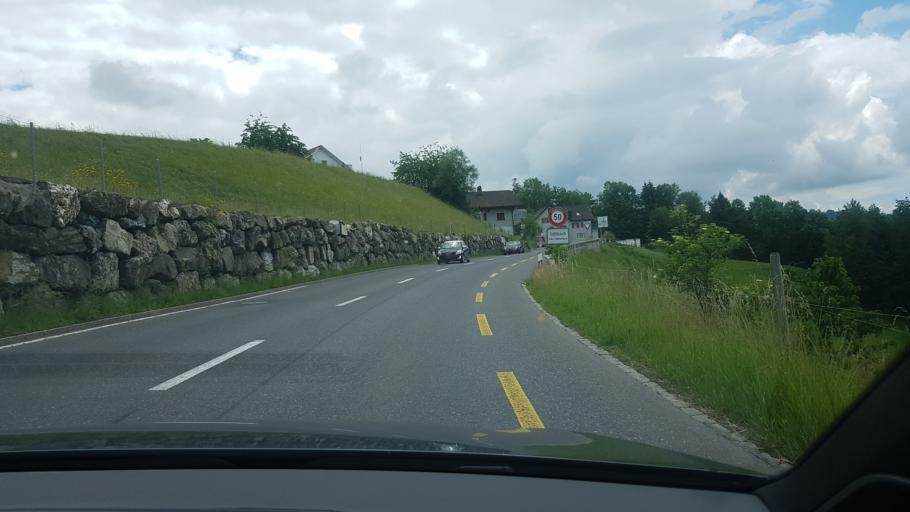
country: CH
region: Zug
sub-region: Zug
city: Menzingen
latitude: 47.1845
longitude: 8.5703
